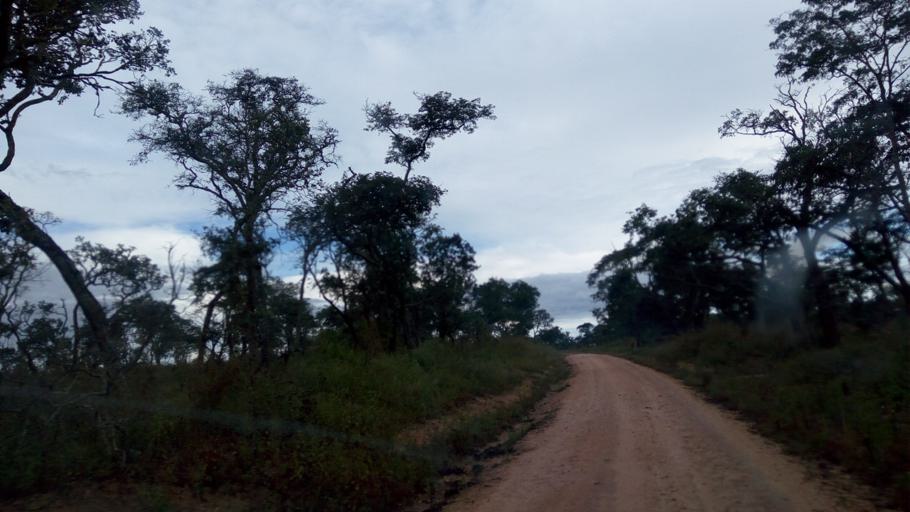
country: CD
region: Katanga
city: Kalemie
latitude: -6.6030
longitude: 29.0422
